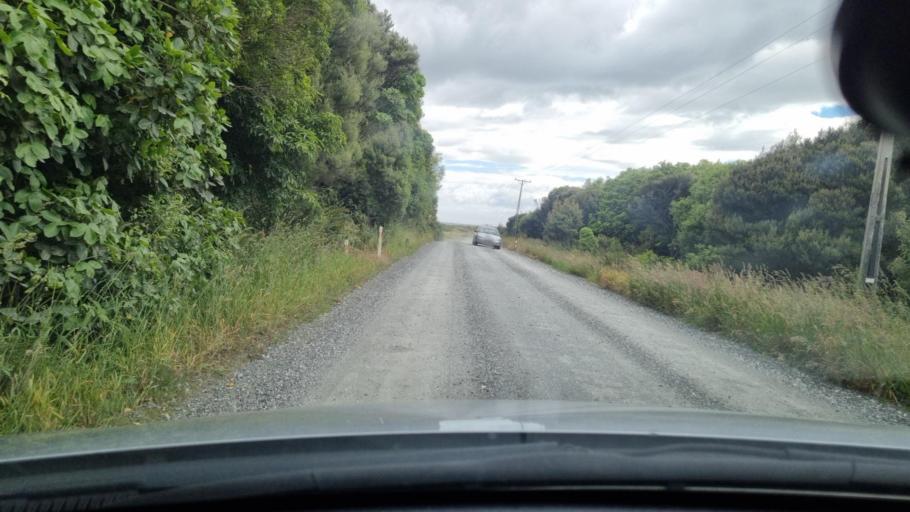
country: NZ
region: Southland
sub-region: Invercargill City
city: Bluff
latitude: -46.5240
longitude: 168.2710
